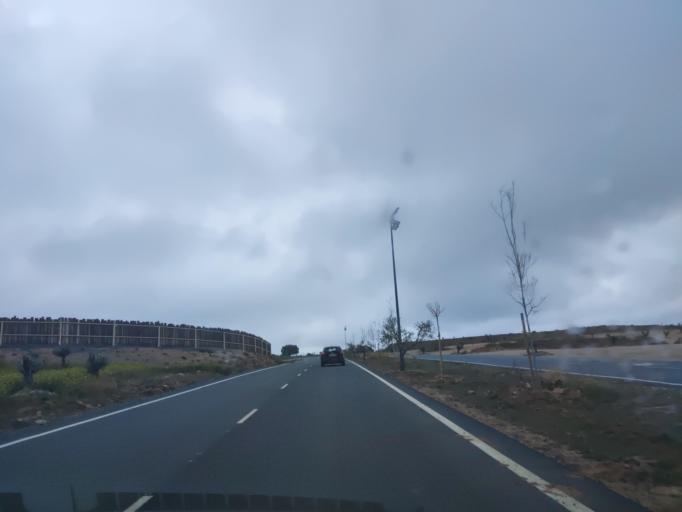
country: ES
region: Castille-La Mancha
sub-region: Province of Toledo
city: Toledo
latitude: 39.8402
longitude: -4.0873
